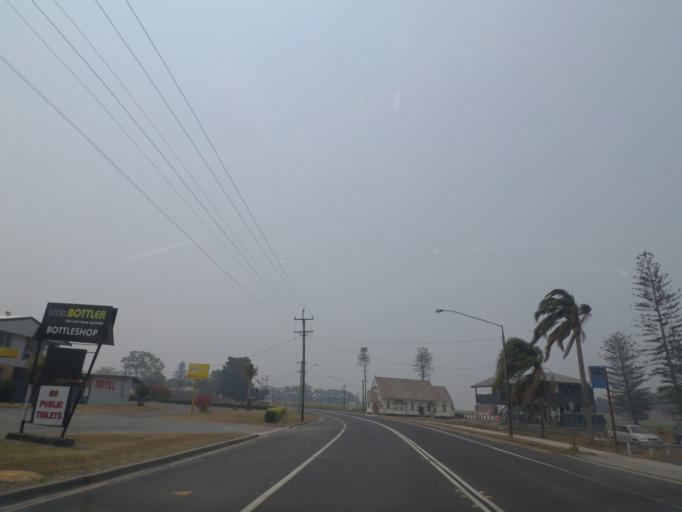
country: AU
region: New South Wales
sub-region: Richmond Valley
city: Evans Head
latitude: -29.0098
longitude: 153.4361
